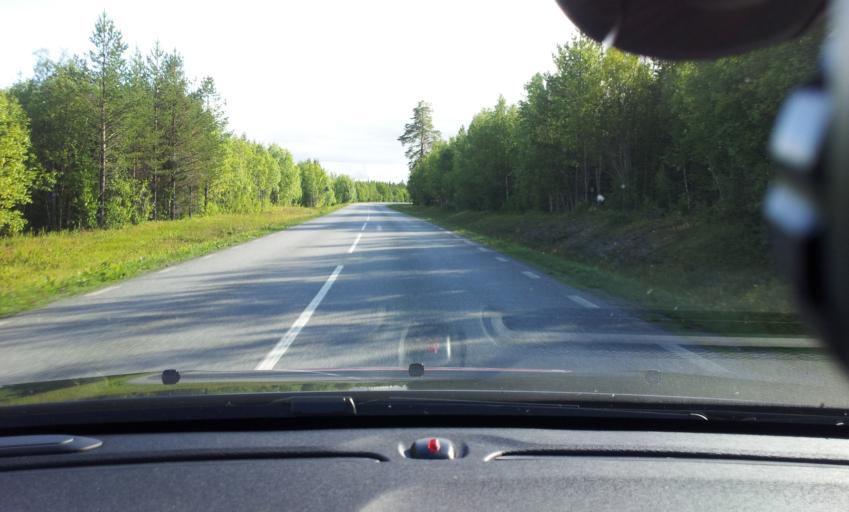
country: SE
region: Jaemtland
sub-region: Krokoms Kommun
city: Krokom
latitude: 63.4709
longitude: 14.1933
